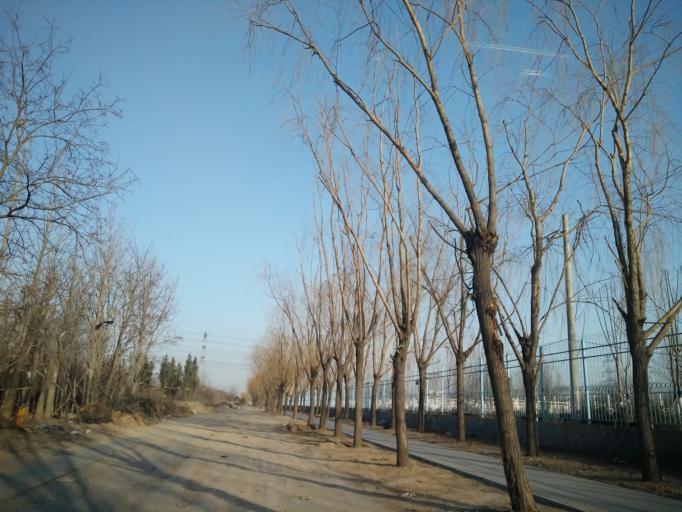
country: CN
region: Beijing
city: Xingfeng
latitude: 39.7214
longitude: 116.3789
